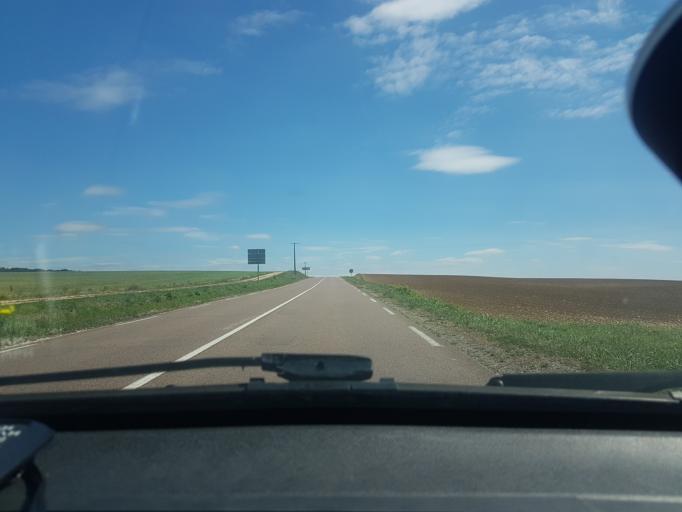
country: FR
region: Bourgogne
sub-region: Departement de la Cote-d'Or
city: Mirebeau-sur-Beze
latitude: 47.4009
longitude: 5.4136
